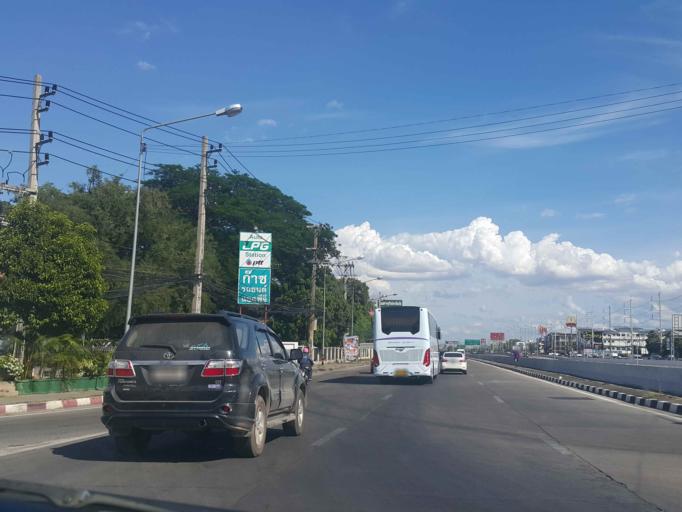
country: TH
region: Chiang Mai
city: Chiang Mai
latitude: 18.8038
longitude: 99.0185
